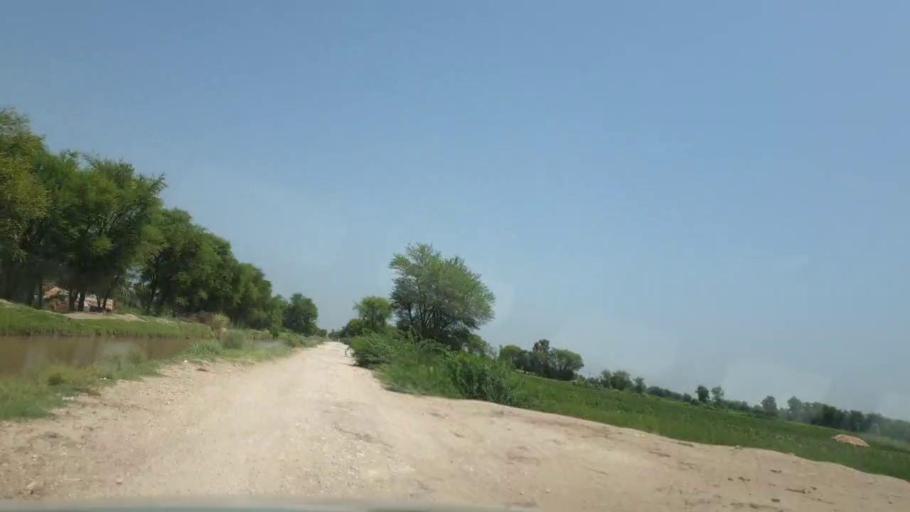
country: PK
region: Sindh
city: Pano Aqil
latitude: 27.6431
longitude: 69.1038
